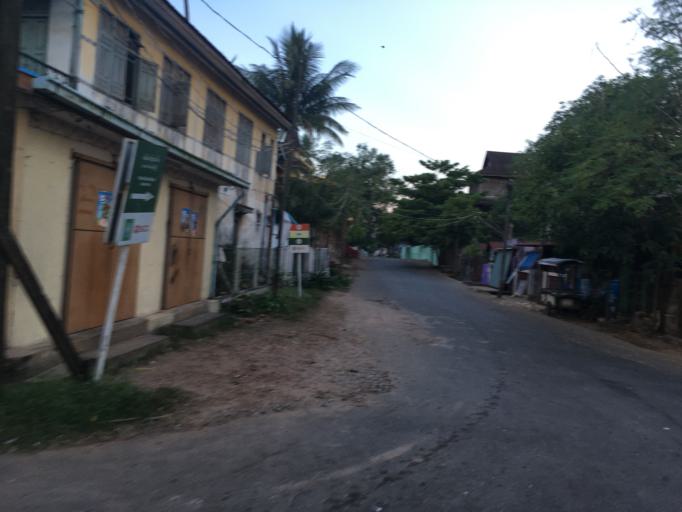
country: MM
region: Mon
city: Mawlamyine
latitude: 16.4750
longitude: 97.6250
